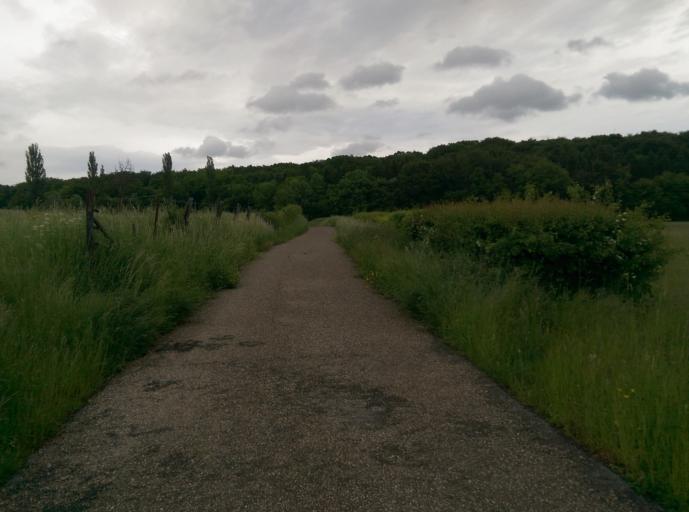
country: LU
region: Luxembourg
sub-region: Canton de Luxembourg
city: Niederanven
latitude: 49.6626
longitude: 6.2560
